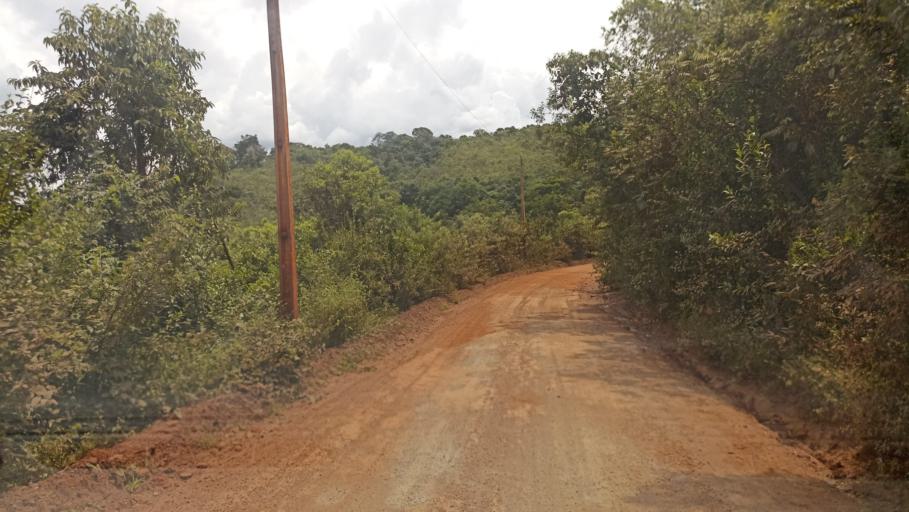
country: BR
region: Minas Gerais
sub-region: Itabirito
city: Itabirito
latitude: -20.3370
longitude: -43.7630
